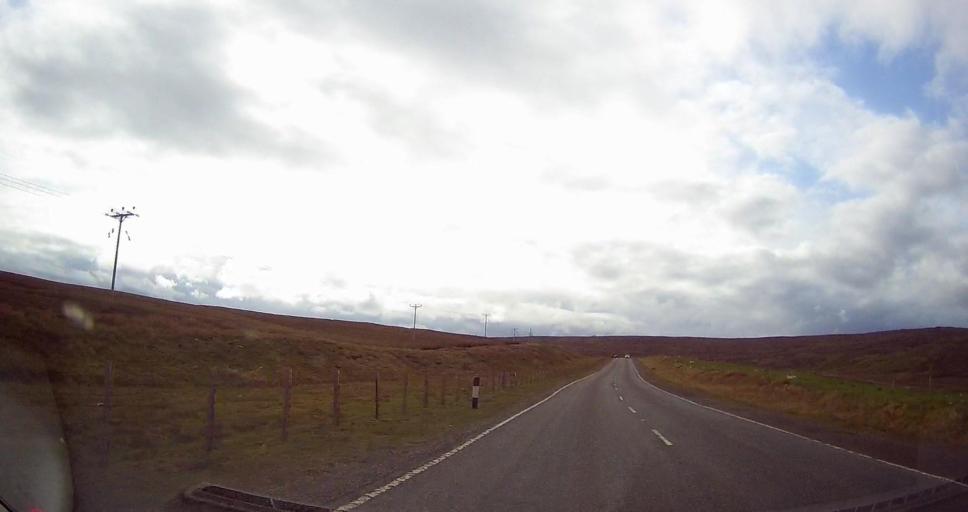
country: GB
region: Scotland
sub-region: Shetland Islands
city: Lerwick
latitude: 60.4436
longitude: -1.2365
